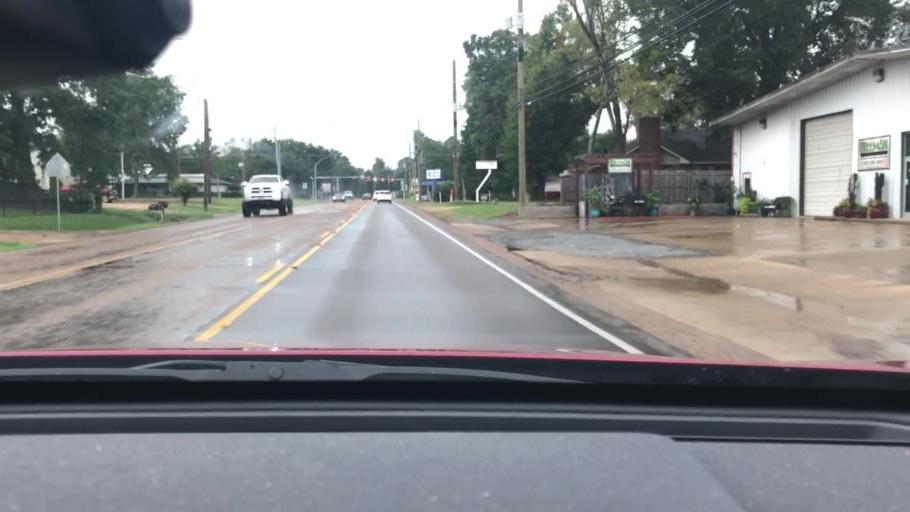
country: US
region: Texas
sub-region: Bowie County
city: Nash
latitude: 33.4425
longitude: -94.1284
